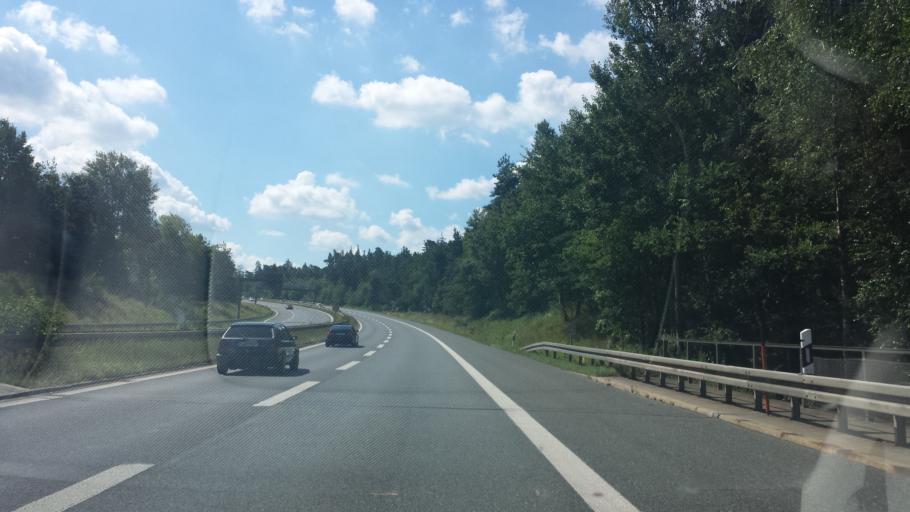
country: DE
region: Bavaria
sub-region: Regierungsbezirk Mittelfranken
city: Feucht
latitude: 49.3556
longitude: 11.2002
